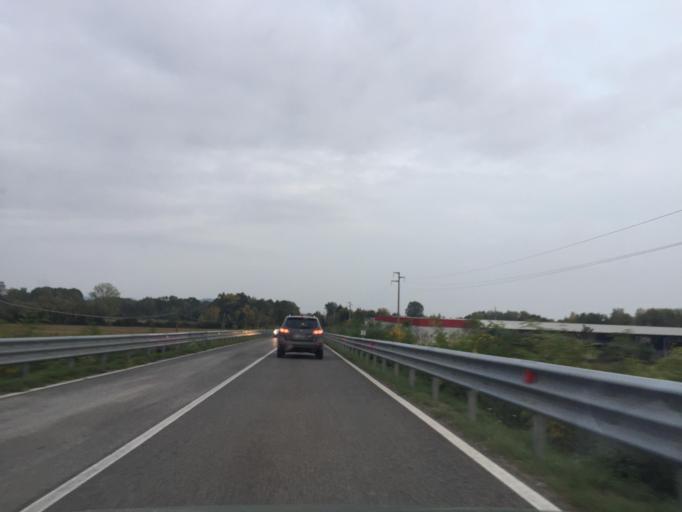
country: IT
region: Friuli Venezia Giulia
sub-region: Provincia di Pordenone
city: Maniago
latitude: 46.1742
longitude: 12.7286
